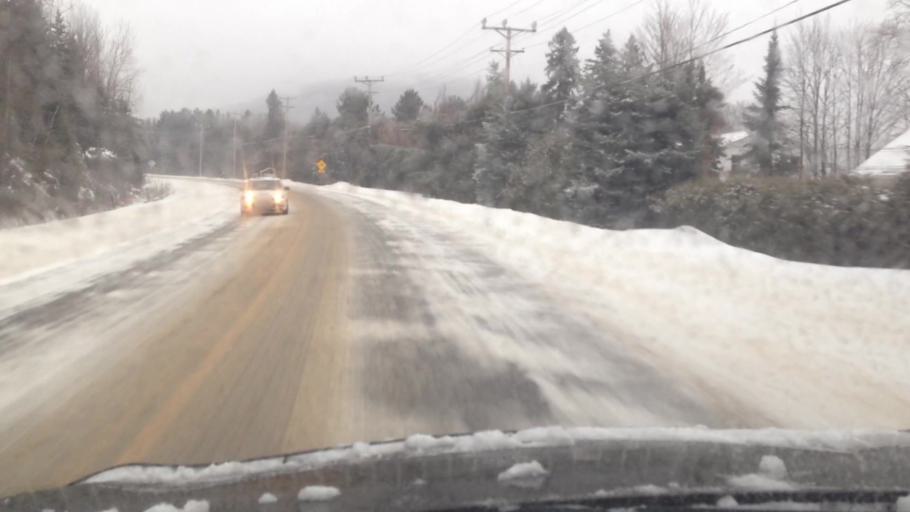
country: CA
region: Quebec
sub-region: Laurentides
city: Mont-Tremblant
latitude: 46.0893
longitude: -74.6083
